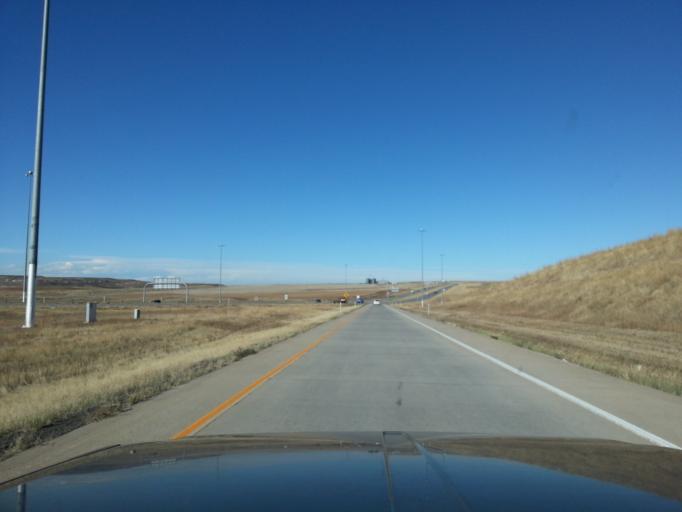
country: US
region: Colorado
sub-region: Adams County
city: Aurora
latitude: 39.8392
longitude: -104.7462
